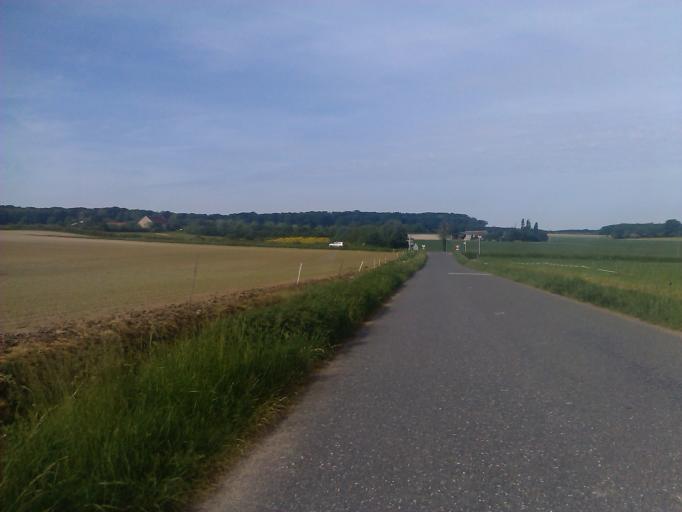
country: FR
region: Auvergne
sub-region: Departement de l'Allier
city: Ainay-le-Chateau
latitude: 46.6091
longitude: 2.7068
